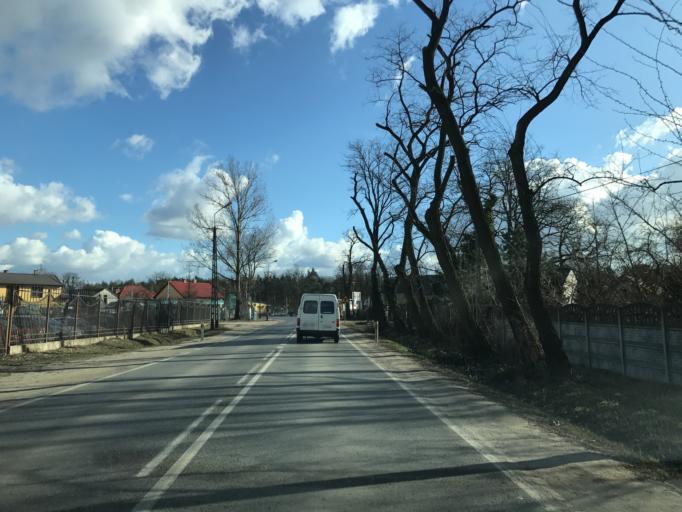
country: PL
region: Masovian Voivodeship
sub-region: Powiat wolominski
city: Radzymin
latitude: 52.3916
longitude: 21.1992
